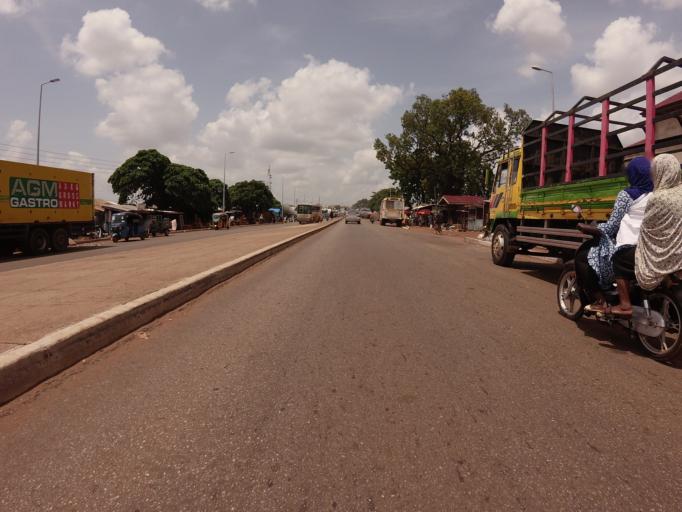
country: GH
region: Northern
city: Tamale
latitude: 9.4043
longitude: -0.8500
